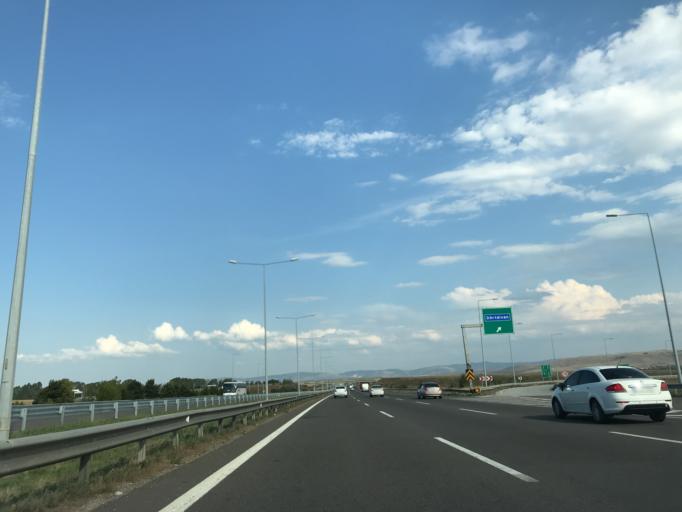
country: TR
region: Bolu
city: Dortdivan
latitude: 40.7446
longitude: 32.1143
